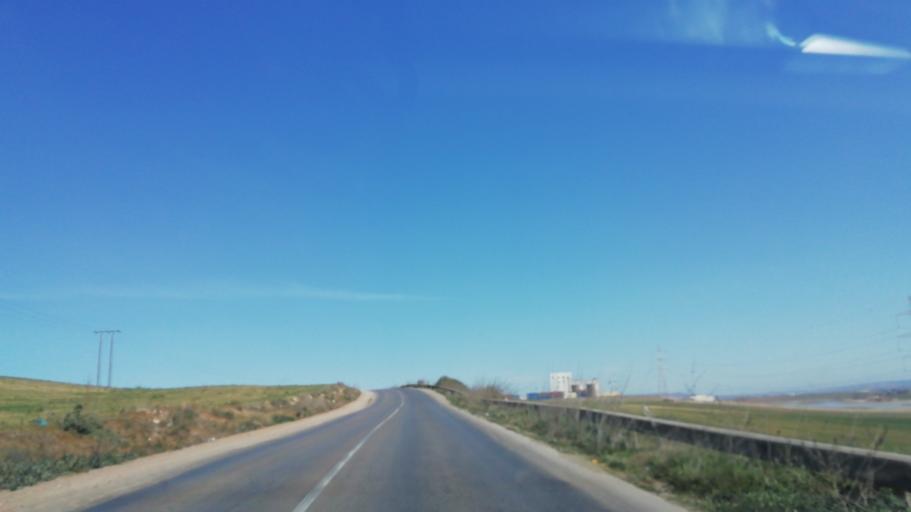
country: DZ
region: Oran
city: Es Senia
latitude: 35.5416
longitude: -0.5833
